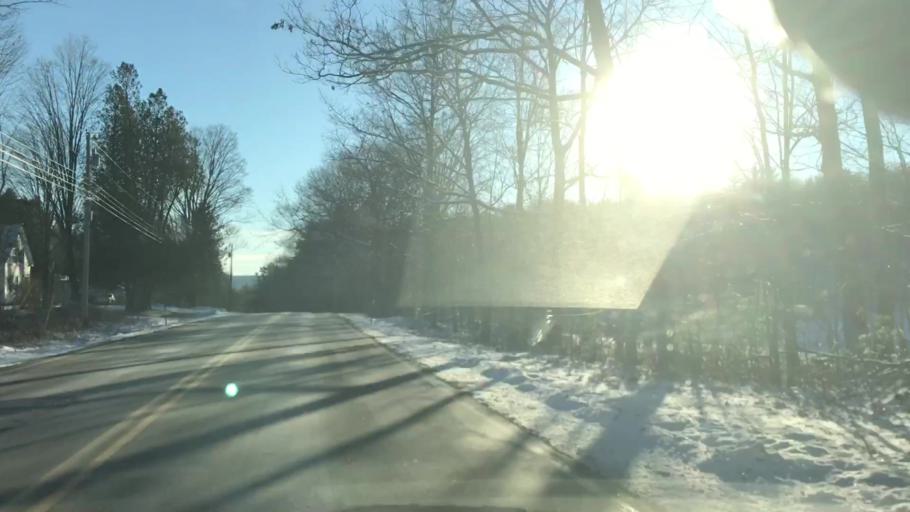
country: US
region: New Hampshire
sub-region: Grafton County
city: Haverhill
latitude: 43.9886
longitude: -72.0791
